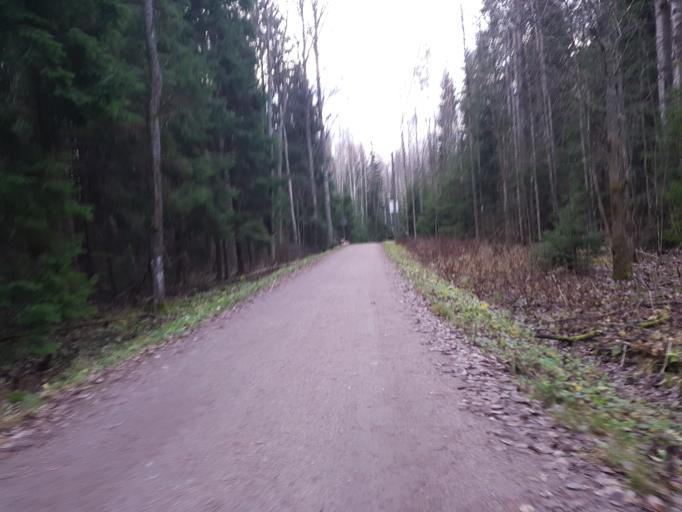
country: FI
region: Uusimaa
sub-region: Helsinki
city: Teekkarikylae
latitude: 60.2700
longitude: 24.9000
